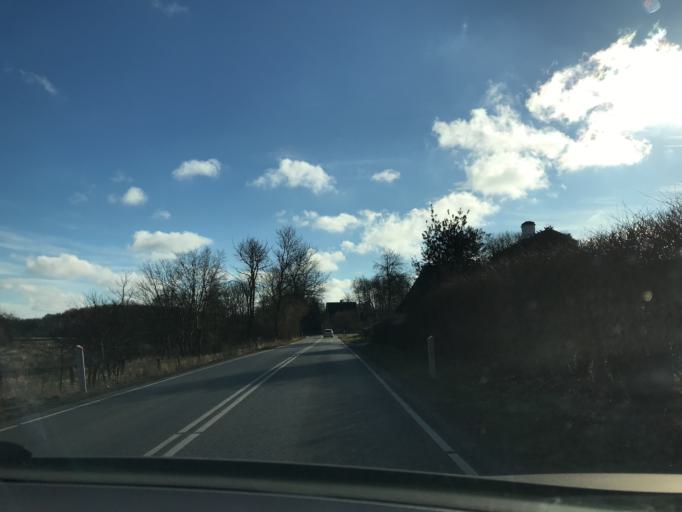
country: DK
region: South Denmark
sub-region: Middelfart Kommune
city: Brenderup
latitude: 55.4965
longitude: 9.9873
